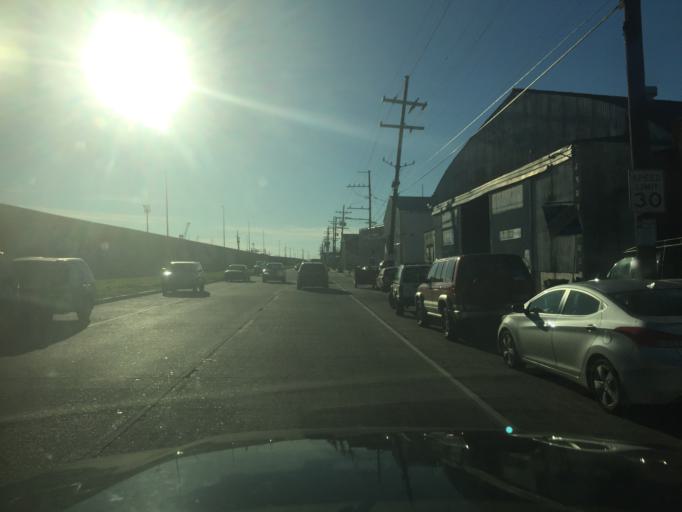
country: US
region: Louisiana
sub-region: Jefferson Parish
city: Harvey
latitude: 29.9204
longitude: -90.0792
